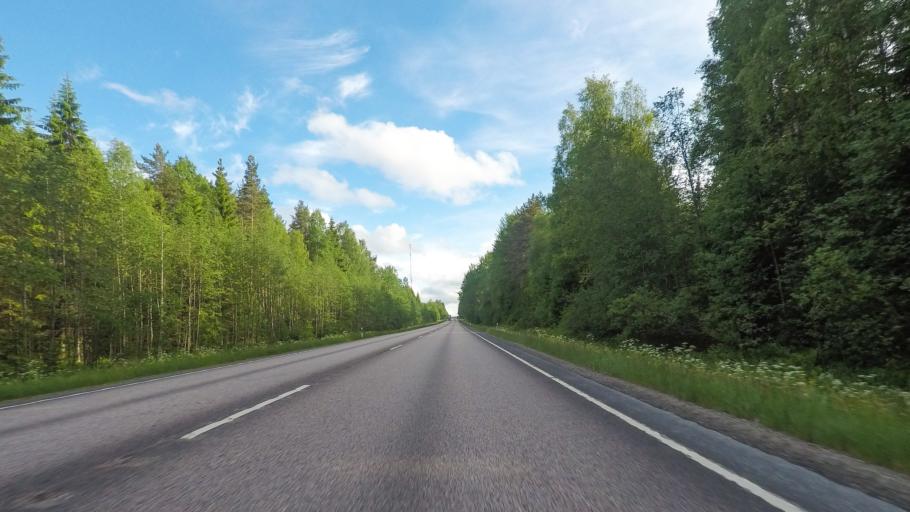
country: FI
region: Central Finland
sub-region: Joutsa
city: Leivonmaeki
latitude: 61.8813
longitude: 26.1116
